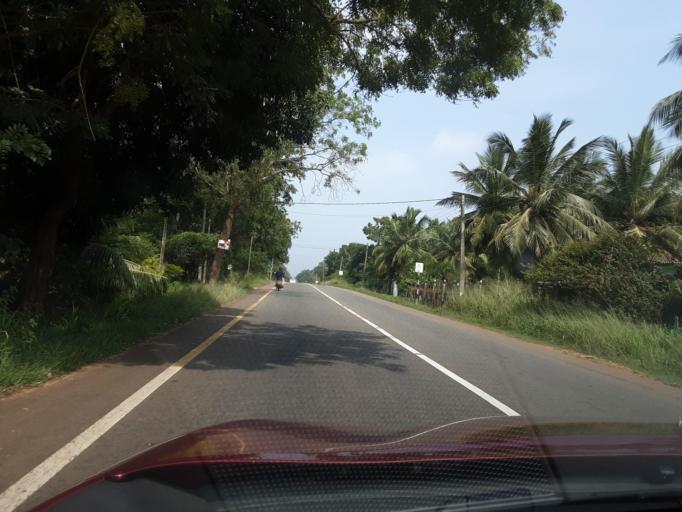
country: LK
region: North Central
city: Anuradhapura
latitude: 8.3255
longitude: 80.5010
